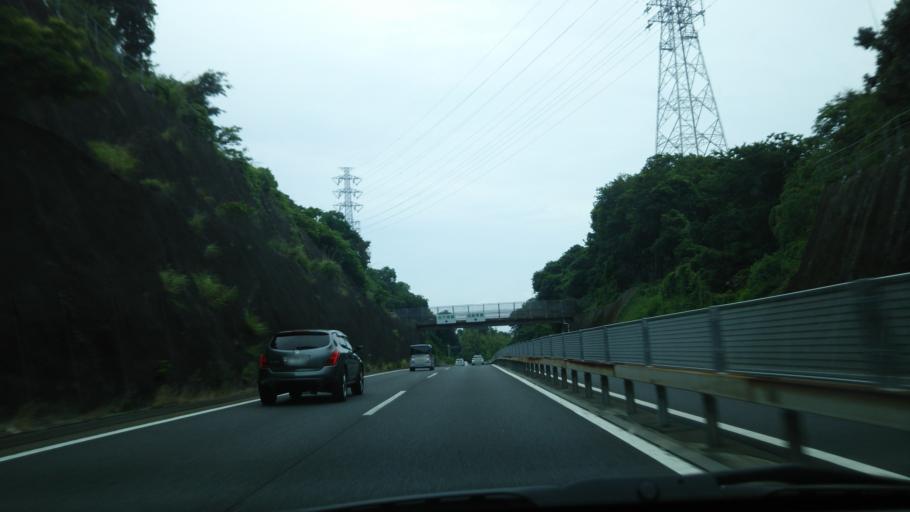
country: JP
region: Kanagawa
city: Oiso
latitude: 35.3266
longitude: 139.2846
